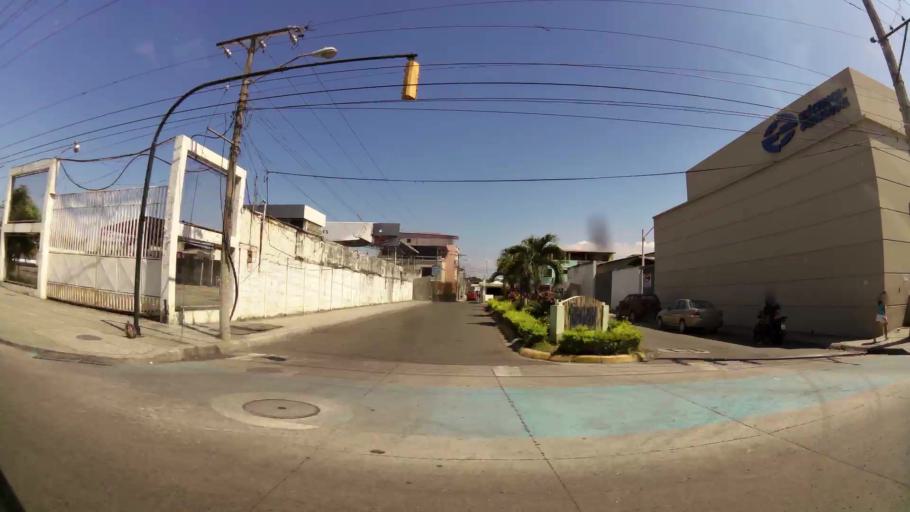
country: EC
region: Guayas
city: Guayaquil
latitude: -2.1905
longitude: -79.9422
